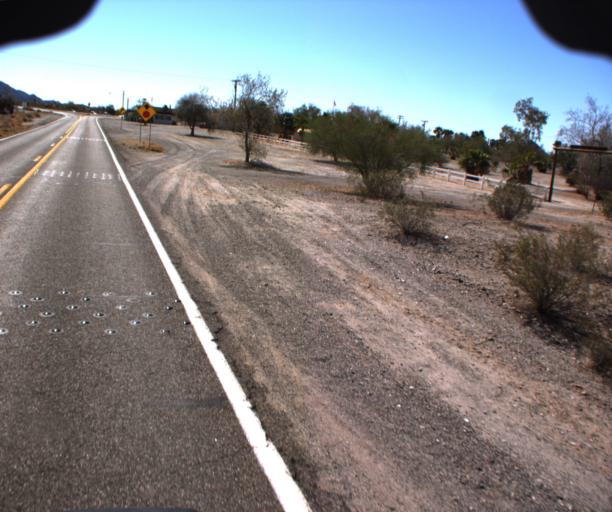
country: US
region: Arizona
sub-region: La Paz County
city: Salome
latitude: 33.7246
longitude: -113.7051
